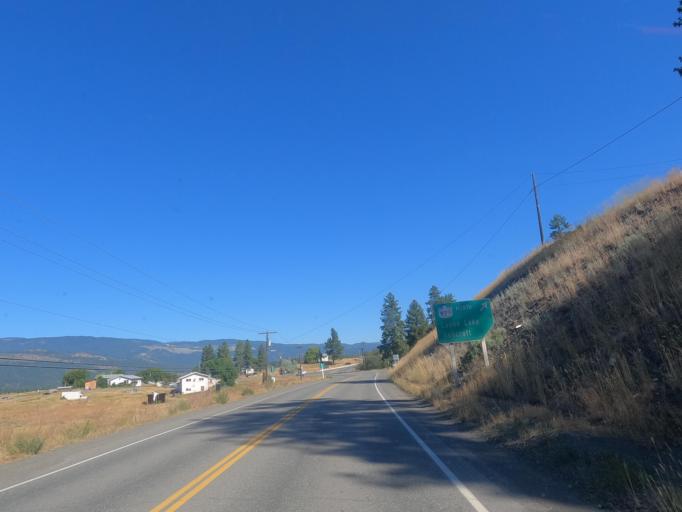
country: CA
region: British Columbia
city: Merritt
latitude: 50.1354
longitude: -120.8365
